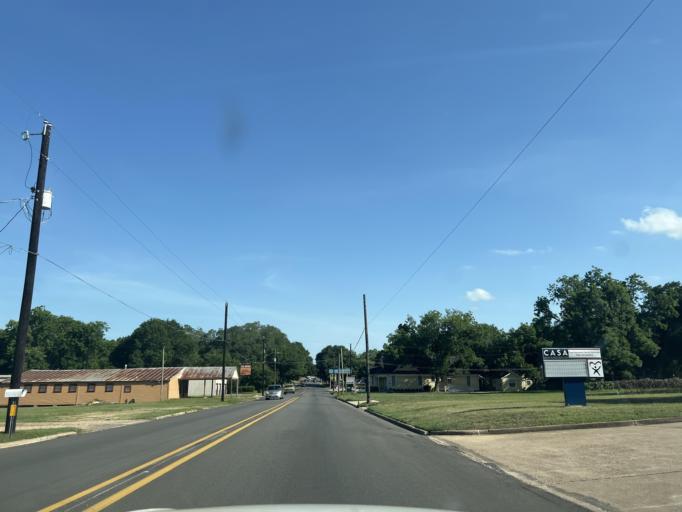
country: US
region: Texas
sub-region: Washington County
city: Brenham
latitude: 30.1551
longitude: -96.3983
